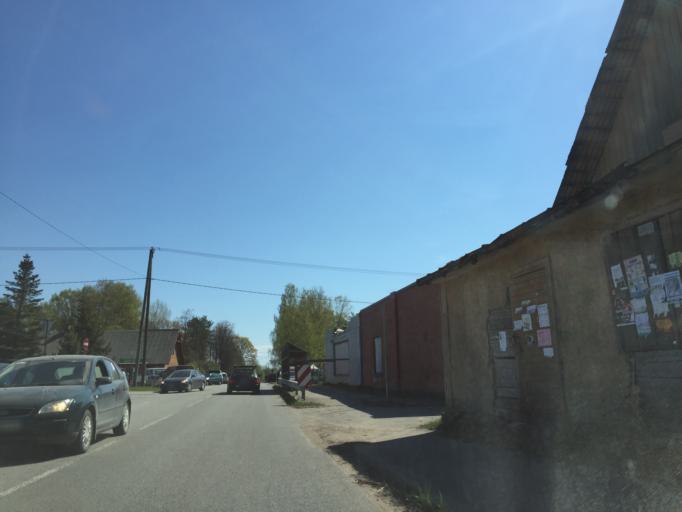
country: LV
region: Saulkrastu
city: Saulkrasti
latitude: 57.3305
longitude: 24.4408
